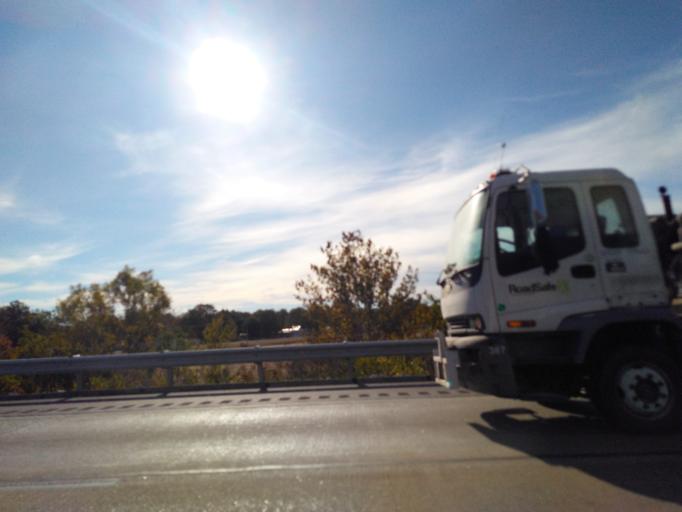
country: US
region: Illinois
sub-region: Saint Clair County
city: Caseyville
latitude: 38.6396
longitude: -90.0534
